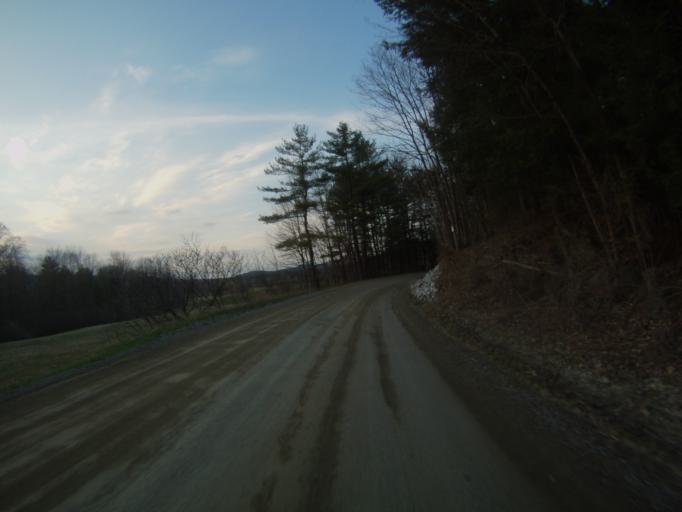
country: US
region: Vermont
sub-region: Addison County
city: Middlebury (village)
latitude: 44.0286
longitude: -73.2206
